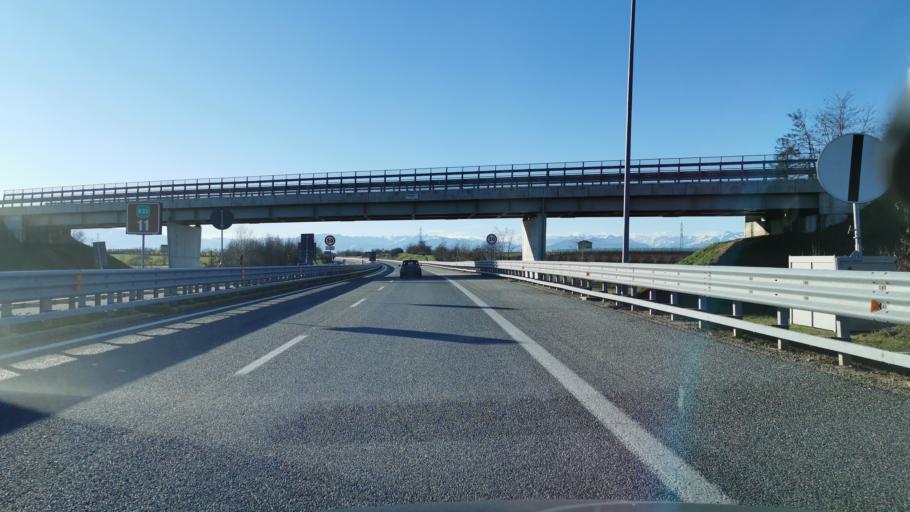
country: IT
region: Piedmont
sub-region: Provincia di Cuneo
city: Magliano Alpi
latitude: 44.4849
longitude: 7.8100
